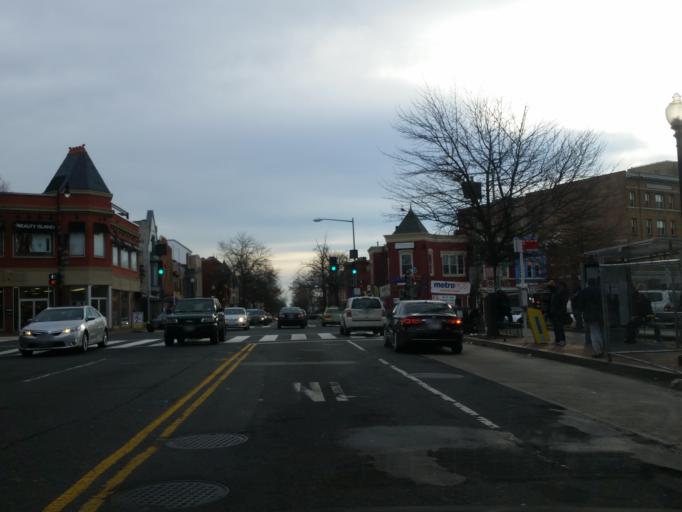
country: US
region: Washington, D.C.
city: Washington, D.C.
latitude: 38.9164
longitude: -77.0224
